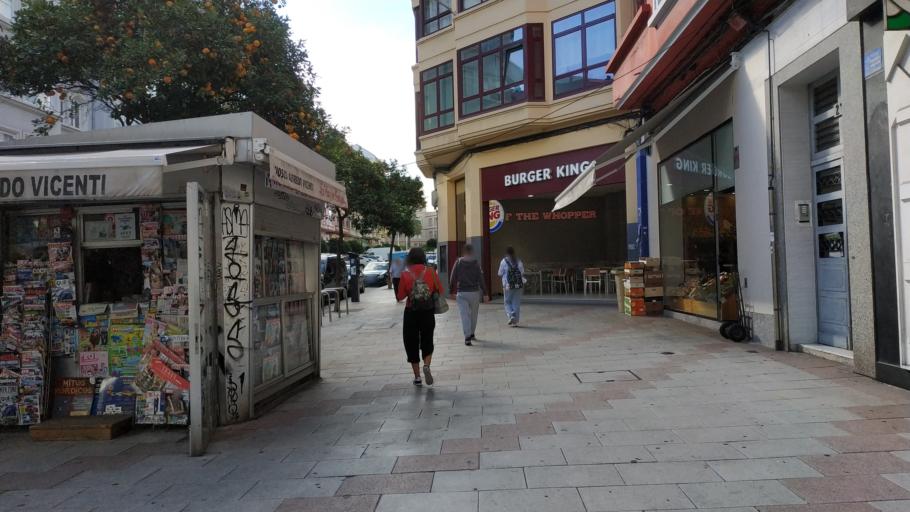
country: ES
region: Galicia
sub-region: Provincia da Coruna
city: A Coruna
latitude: 43.3671
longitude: -8.4117
